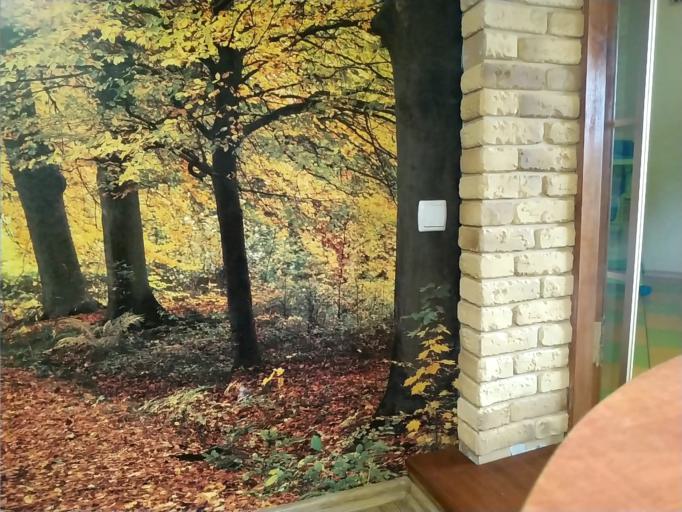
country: RU
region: Smolensk
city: Dorogobuzh
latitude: 54.8645
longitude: 33.3135
